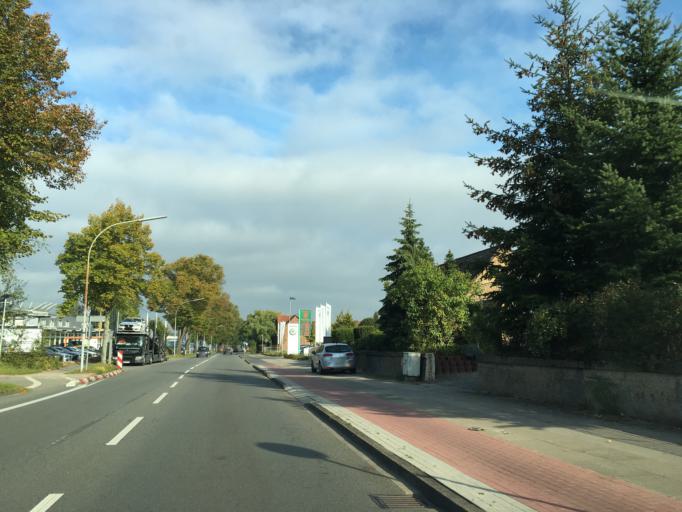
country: DE
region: Lower Saxony
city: Lueneburg
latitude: 53.2651
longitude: 10.4066
